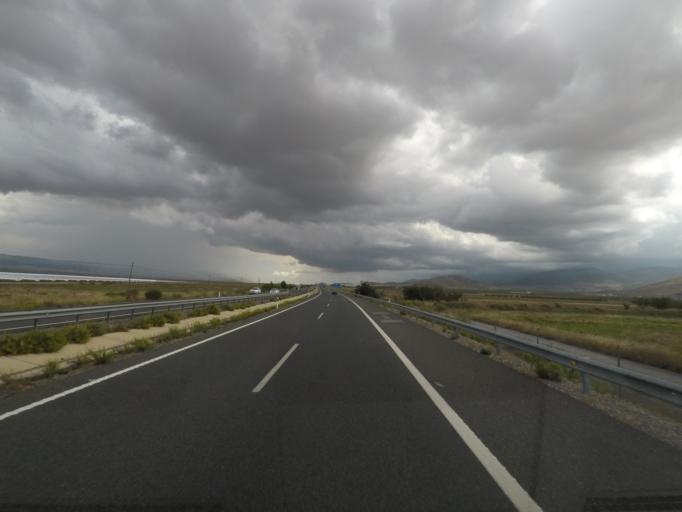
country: ES
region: Andalusia
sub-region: Provincia de Granada
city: Ferreira
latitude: 37.2105
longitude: -3.0652
